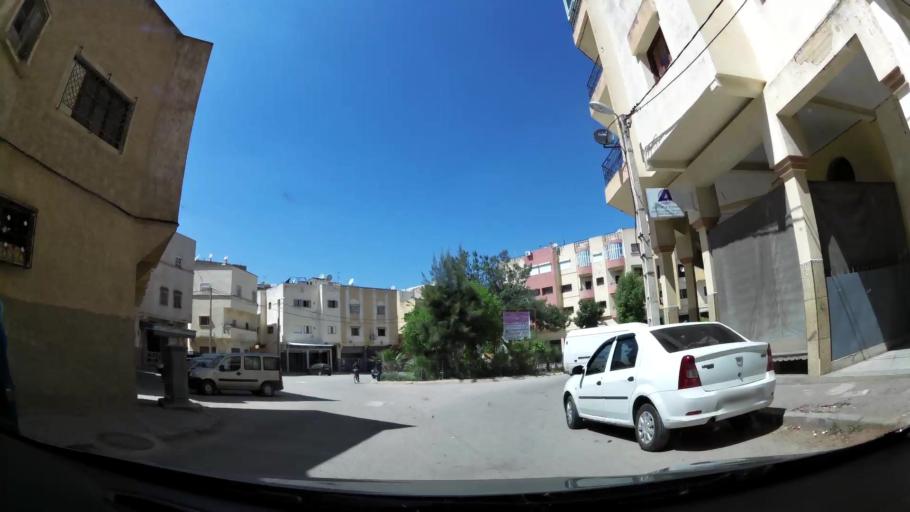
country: MA
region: Fes-Boulemane
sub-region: Fes
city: Fes
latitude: 34.0118
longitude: -5.0260
